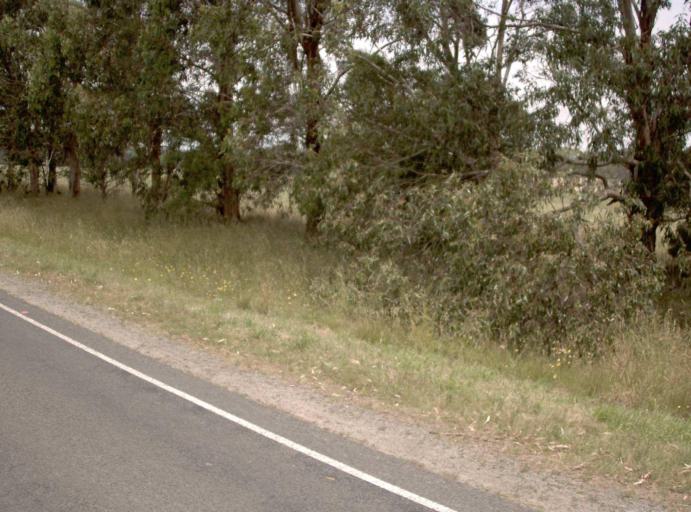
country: AU
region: Victoria
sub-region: Latrobe
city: Traralgon
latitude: -38.4957
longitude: 146.7122
